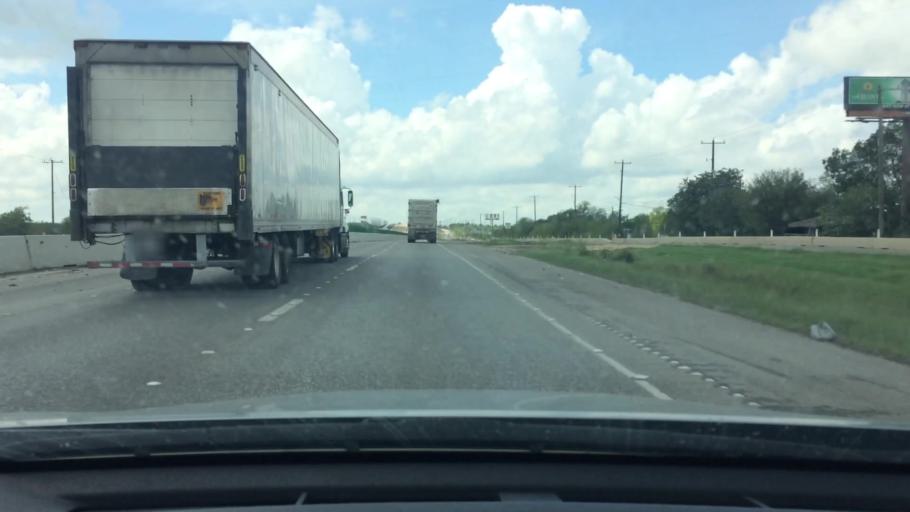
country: US
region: Texas
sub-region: Bexar County
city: Kirby
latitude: 29.4534
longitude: -98.3351
